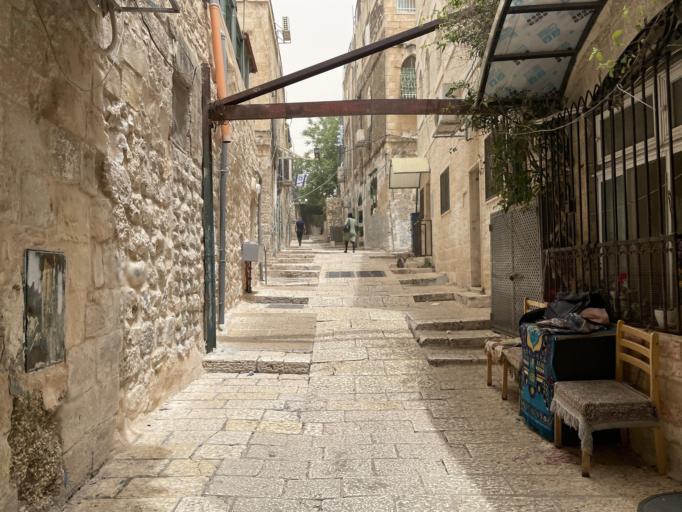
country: PS
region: West Bank
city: East Jerusalem
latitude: 31.7819
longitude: 35.2332
